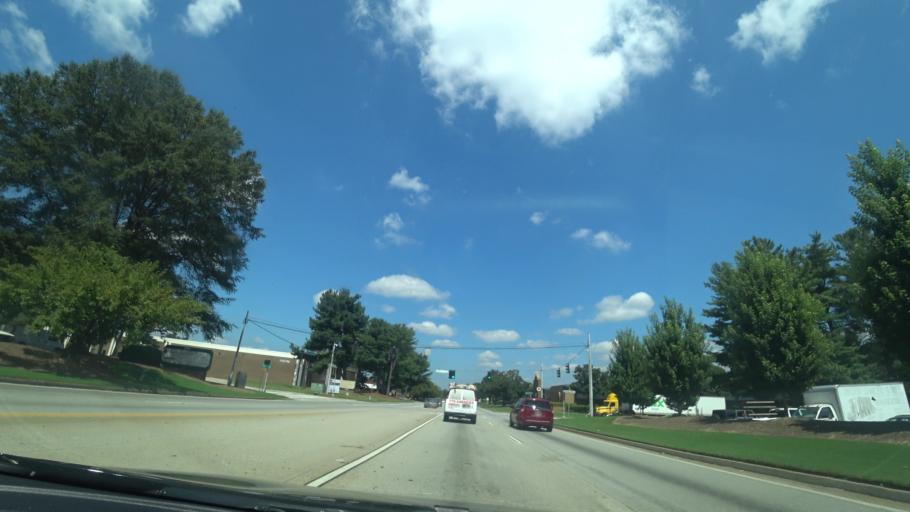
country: US
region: Georgia
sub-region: Gwinnett County
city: Norcross
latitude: 33.9392
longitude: -84.2365
